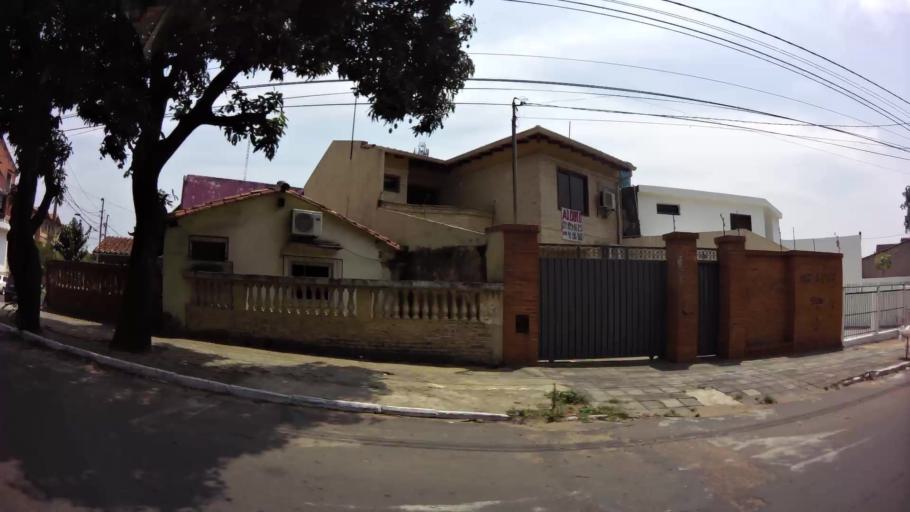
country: PY
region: Asuncion
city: Asuncion
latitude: -25.2689
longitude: -57.5976
